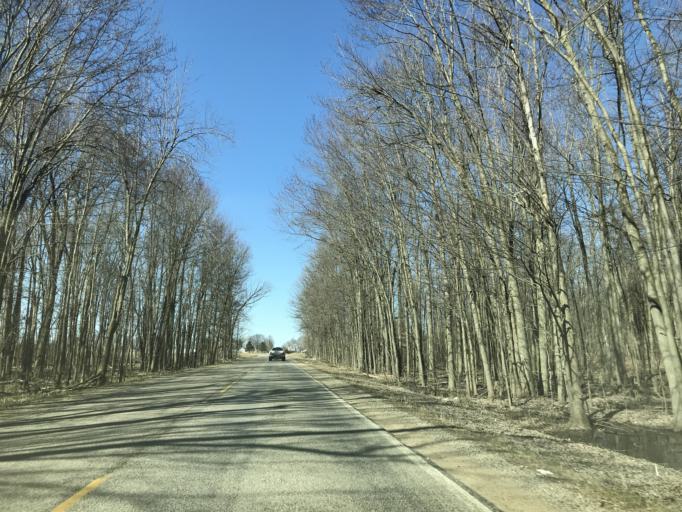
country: US
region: Michigan
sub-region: Hillsdale County
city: Litchfield
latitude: 41.9857
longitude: -84.7900
